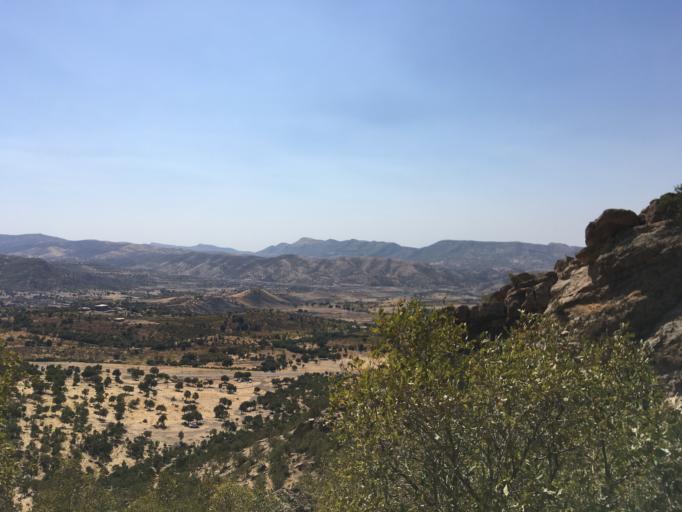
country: IQ
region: Arbil
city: Nahiyat Hiran
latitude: 36.3061
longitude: 44.4165
